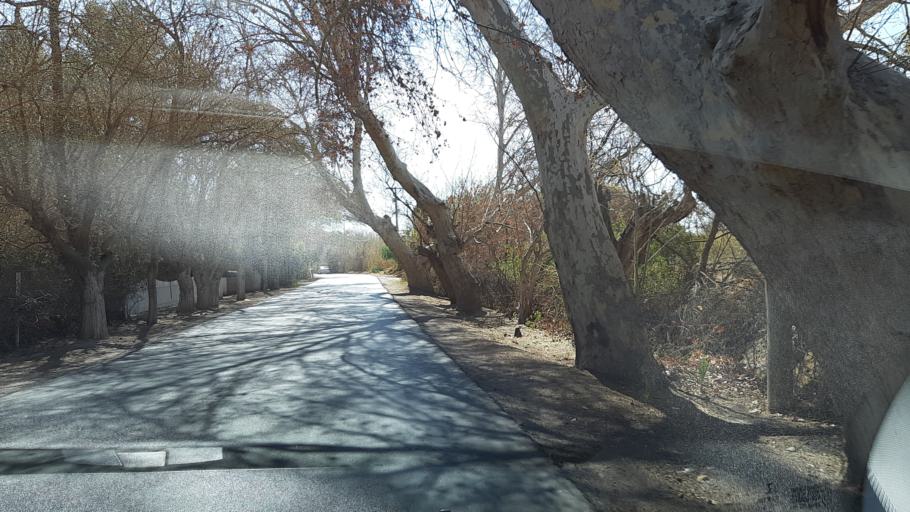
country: AR
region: San Juan
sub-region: Departamento de Rivadavia
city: Rivadavia
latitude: -31.5266
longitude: -68.6194
